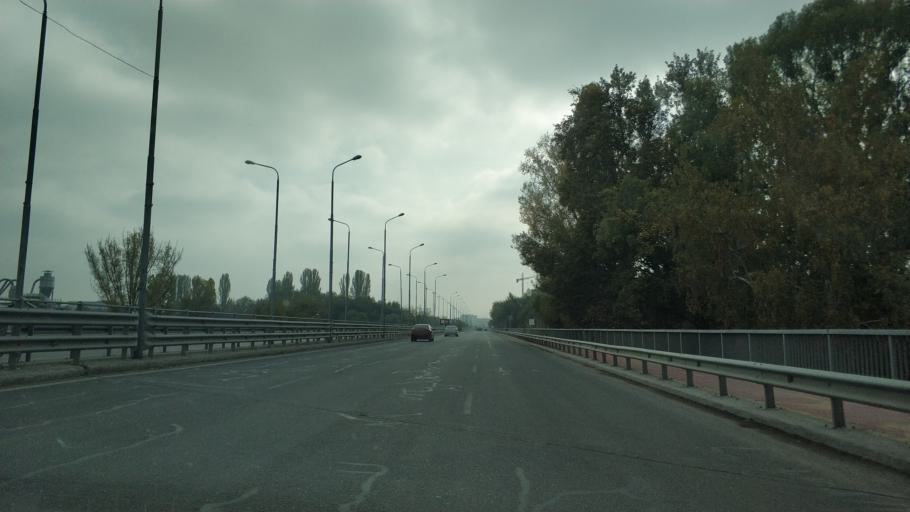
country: BG
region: Plovdiv
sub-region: Obshtina Plovdiv
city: Plovdiv
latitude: 42.1586
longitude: 24.7649
